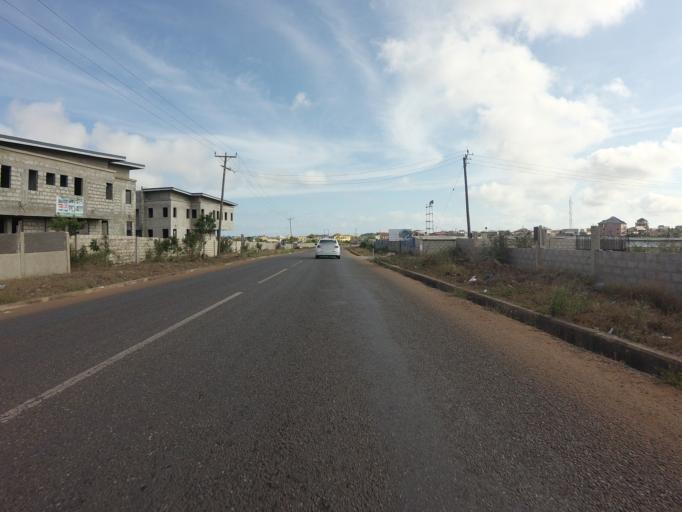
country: GH
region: Greater Accra
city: Teshi Old Town
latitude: 5.5914
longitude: -0.1362
